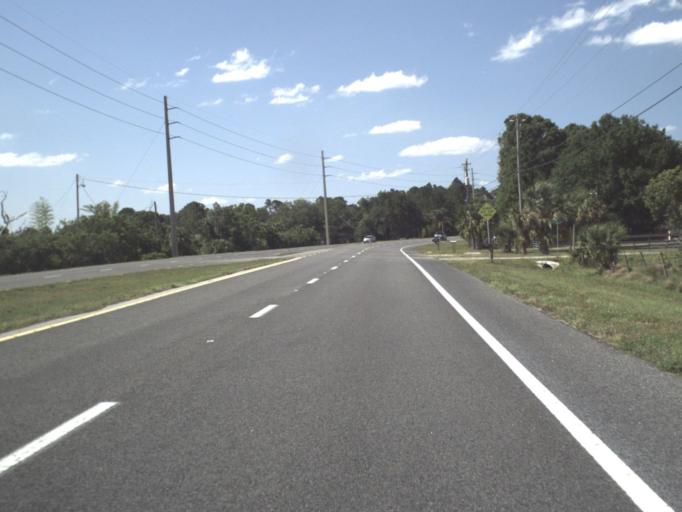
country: US
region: Florida
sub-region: Volusia County
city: Oak Hill
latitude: 28.7848
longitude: -80.8831
